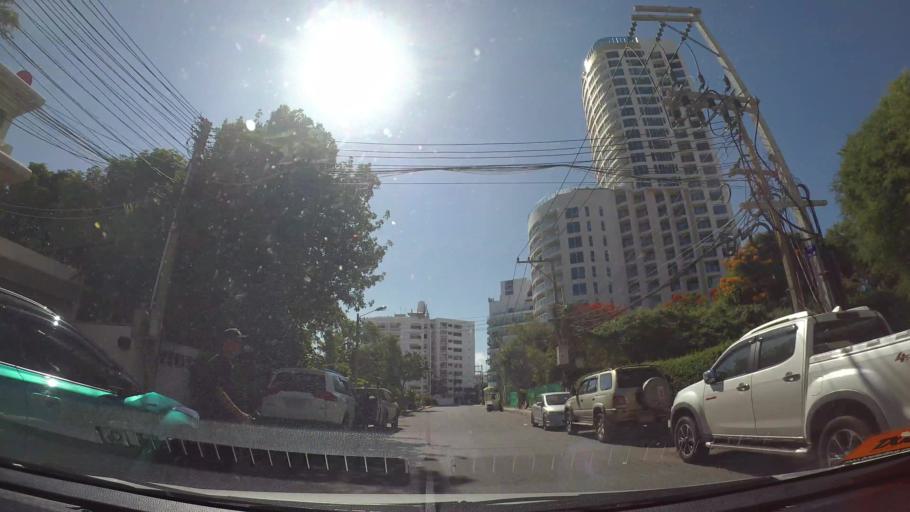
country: TH
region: Chon Buri
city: Phatthaya
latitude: 12.9098
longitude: 100.8576
